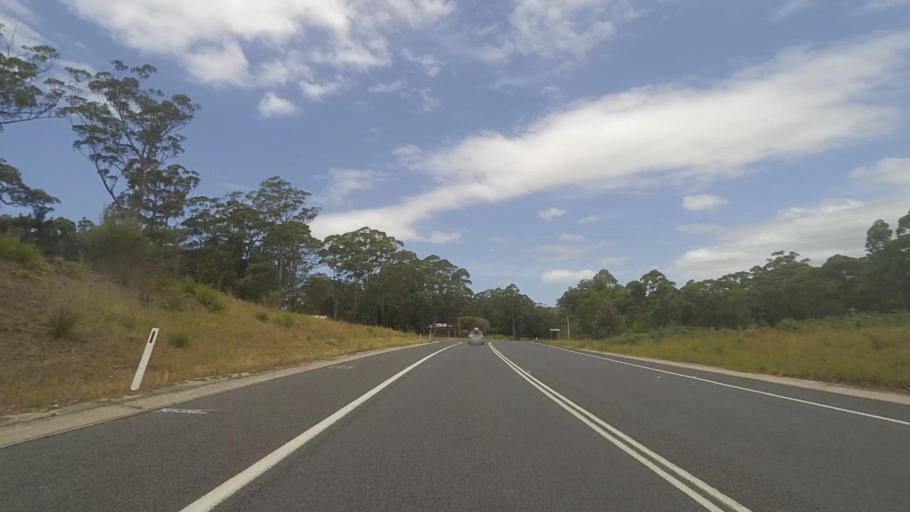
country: AU
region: New South Wales
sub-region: Shoalhaven Shire
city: Milton
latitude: -35.2220
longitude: 150.4358
